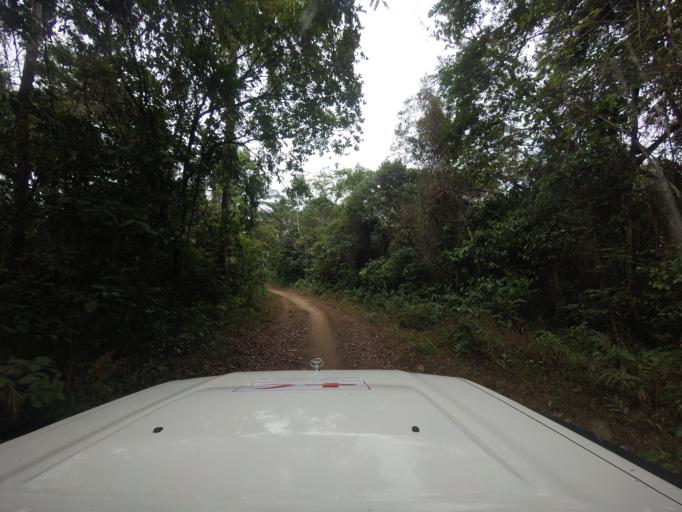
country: SL
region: Eastern Province
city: Buedu
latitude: 8.2397
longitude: -10.2631
